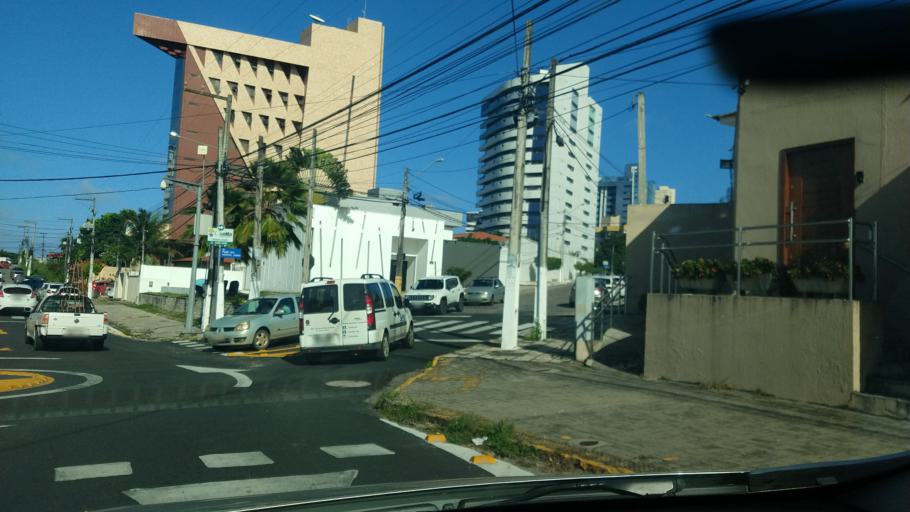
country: BR
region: Rio Grande do Norte
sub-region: Natal
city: Natal
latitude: -5.8328
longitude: -35.2151
